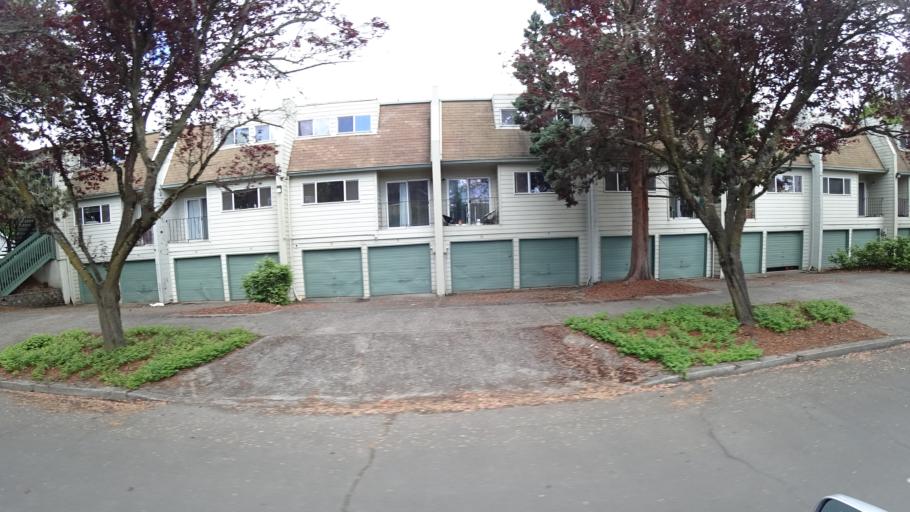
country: US
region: Oregon
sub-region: Multnomah County
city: Portland
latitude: 45.5010
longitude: -122.6466
